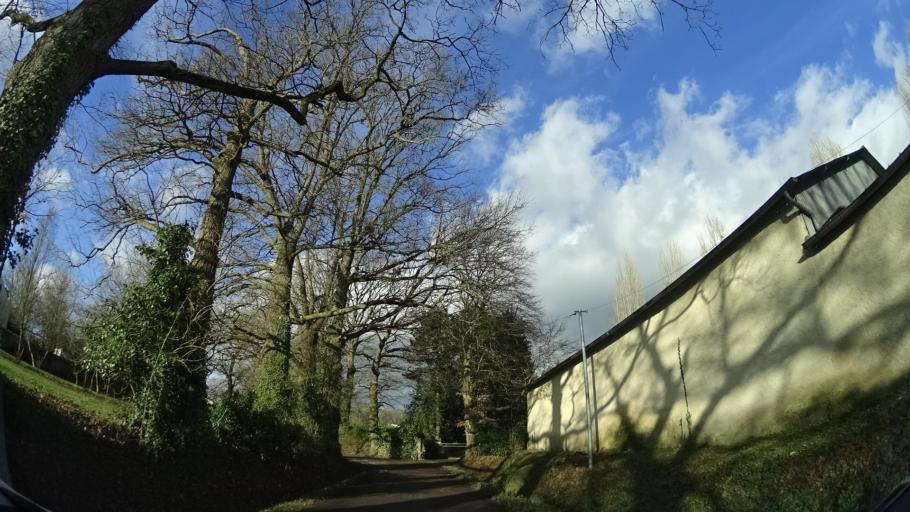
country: FR
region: Brittany
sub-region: Departement d'Ille-et-Vilaine
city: Cesson-Sevigne
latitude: 48.1336
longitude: -1.6355
